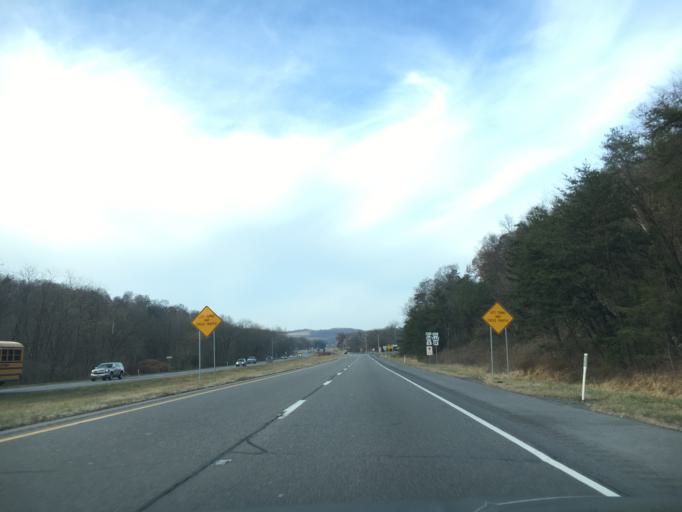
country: US
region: Pennsylvania
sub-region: Montour County
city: Danville
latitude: 40.9799
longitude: -76.6252
